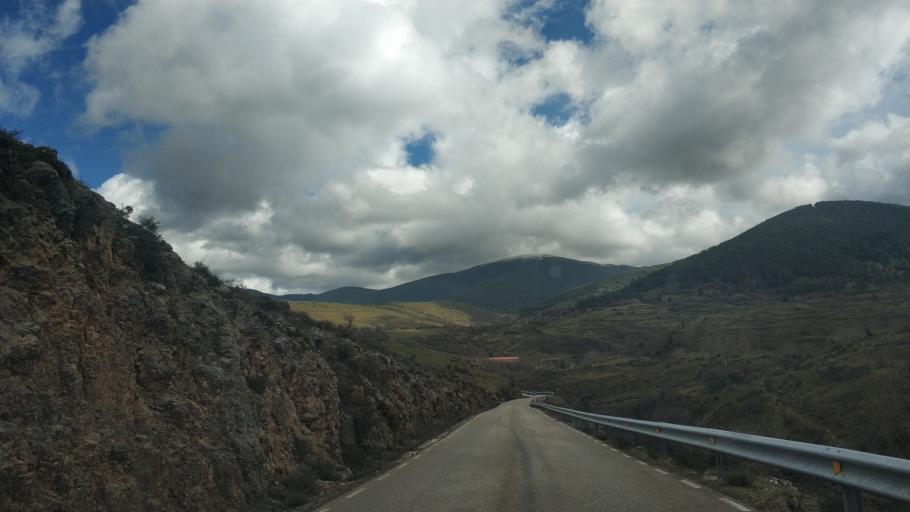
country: ES
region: Castille and Leon
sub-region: Provincia de Burgos
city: Neila
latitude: 42.0585
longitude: -2.9988
